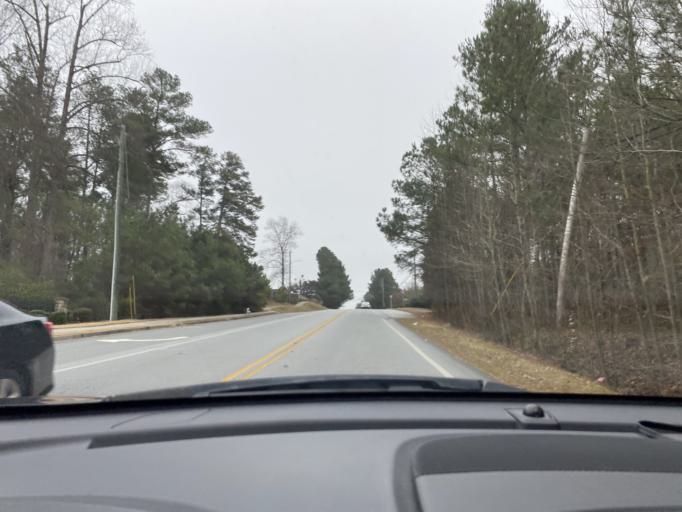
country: US
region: Georgia
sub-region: Gwinnett County
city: Grayson
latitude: 33.9085
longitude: -83.9280
